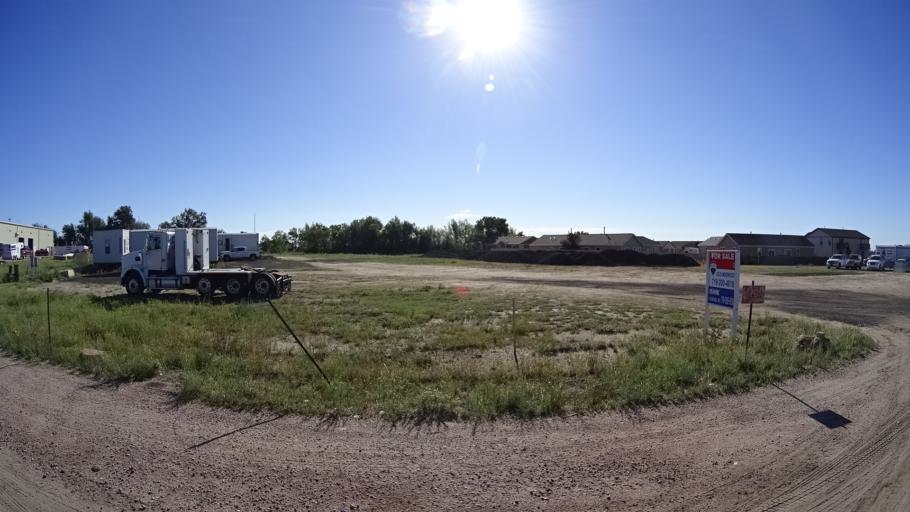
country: US
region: Colorado
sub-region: El Paso County
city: Cimarron Hills
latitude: 38.9323
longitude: -104.6085
